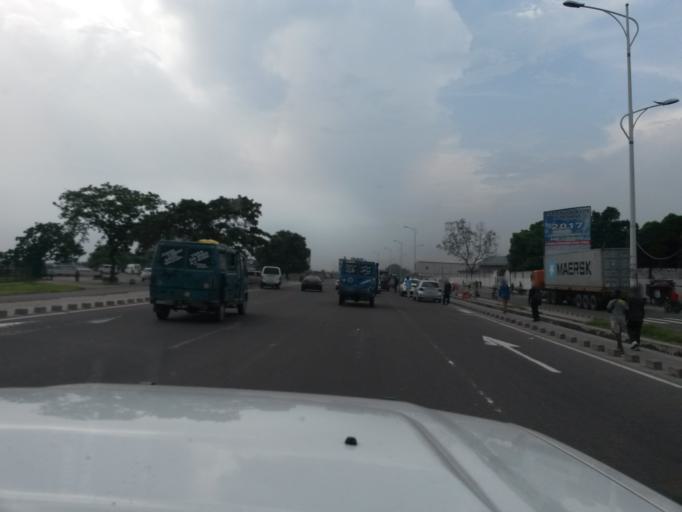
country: CD
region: Kinshasa
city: Masina
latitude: -4.3741
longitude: 15.3465
